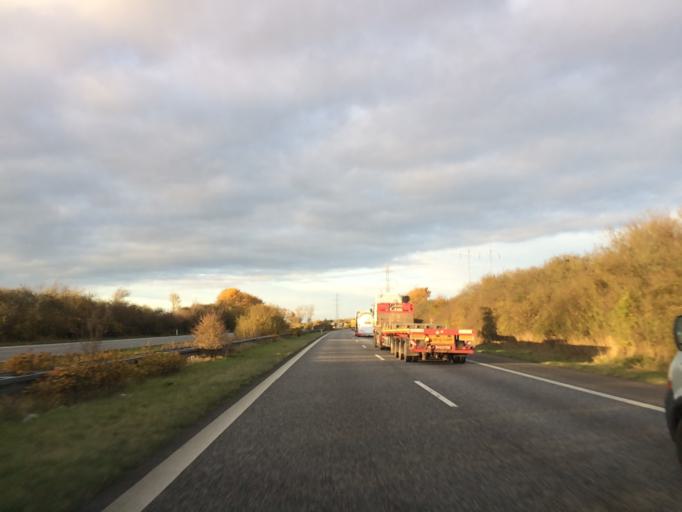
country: DK
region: South Denmark
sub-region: Aabenraa Kommune
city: Rodekro
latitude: 55.0442
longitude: 9.3527
